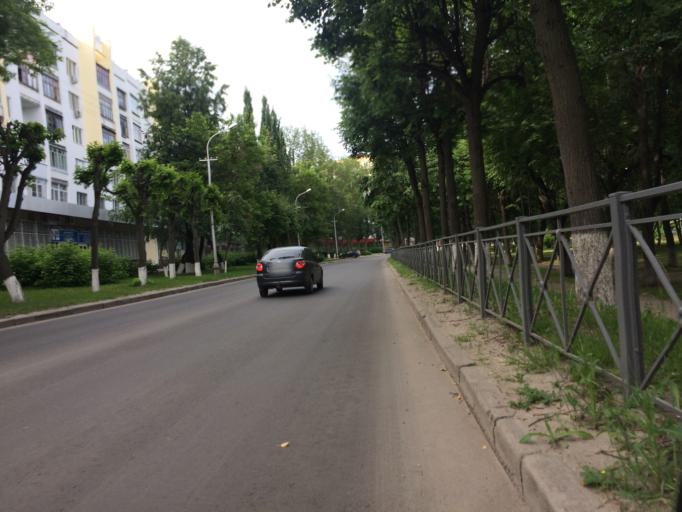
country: RU
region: Mariy-El
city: Yoshkar-Ola
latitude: 56.6270
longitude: 47.8915
